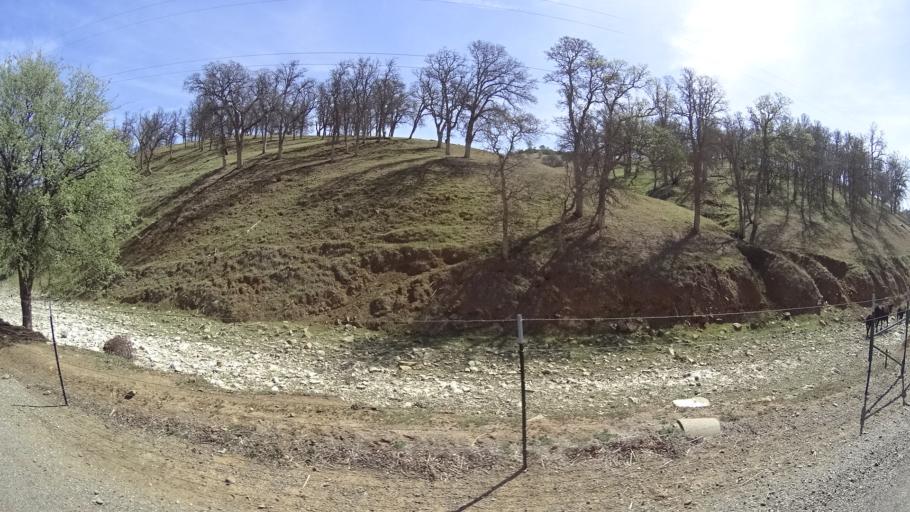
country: US
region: California
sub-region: Glenn County
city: Willows
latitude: 39.4732
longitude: -122.4490
